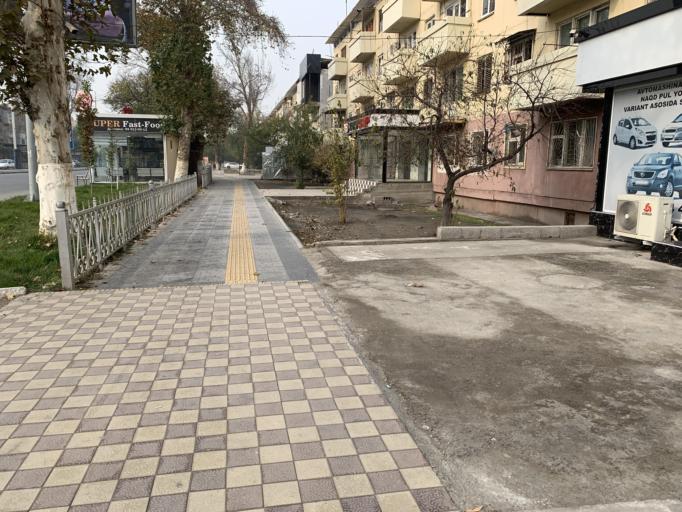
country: UZ
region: Fergana
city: Qo`qon
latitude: 40.5442
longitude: 70.9335
